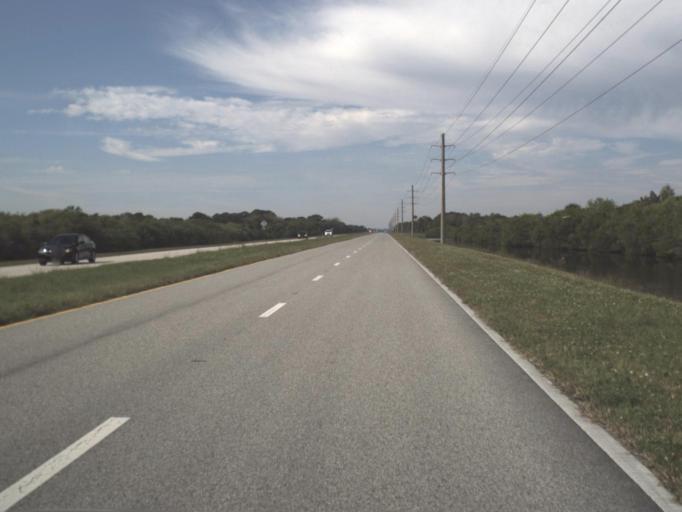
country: US
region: Florida
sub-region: Brevard County
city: Merritt Island
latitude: 28.5264
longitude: -80.7069
